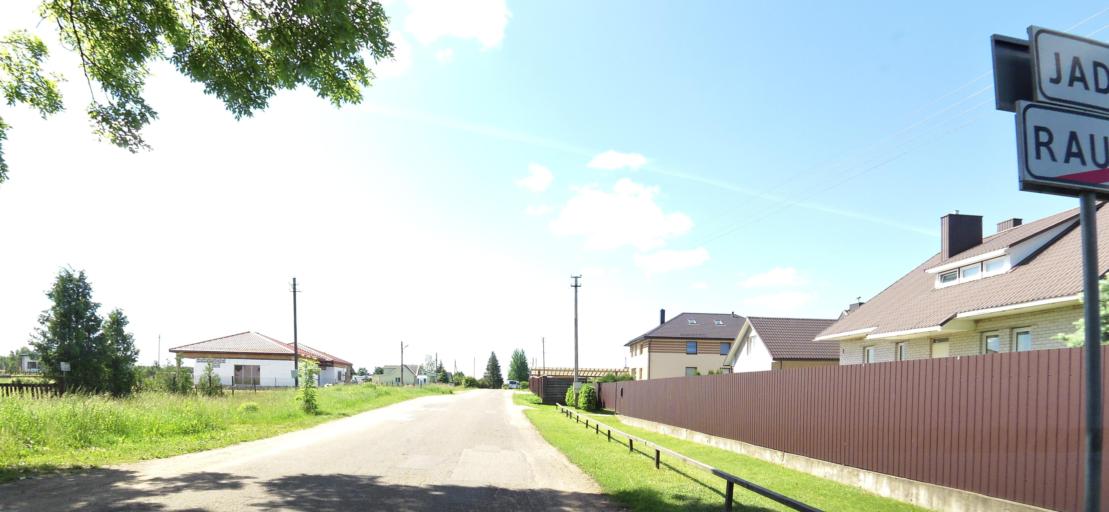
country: LT
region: Vilnius County
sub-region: Vilnius
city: Fabijoniskes
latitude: 54.8248
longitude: 25.2807
